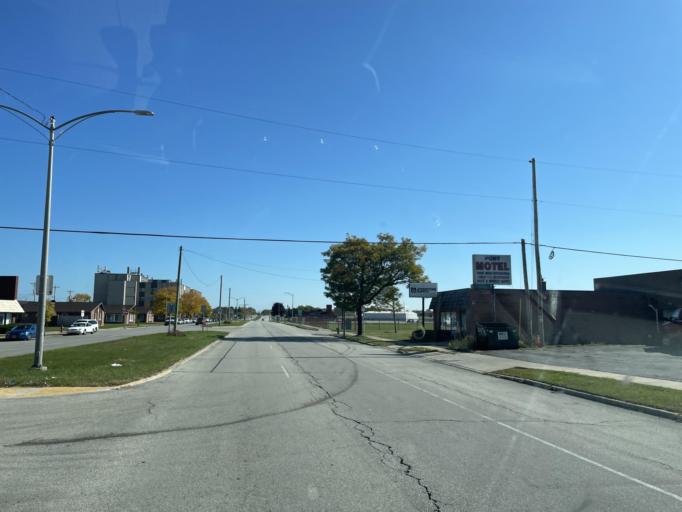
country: US
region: Wisconsin
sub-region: Waukesha County
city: Butler
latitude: 43.1188
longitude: -88.0340
